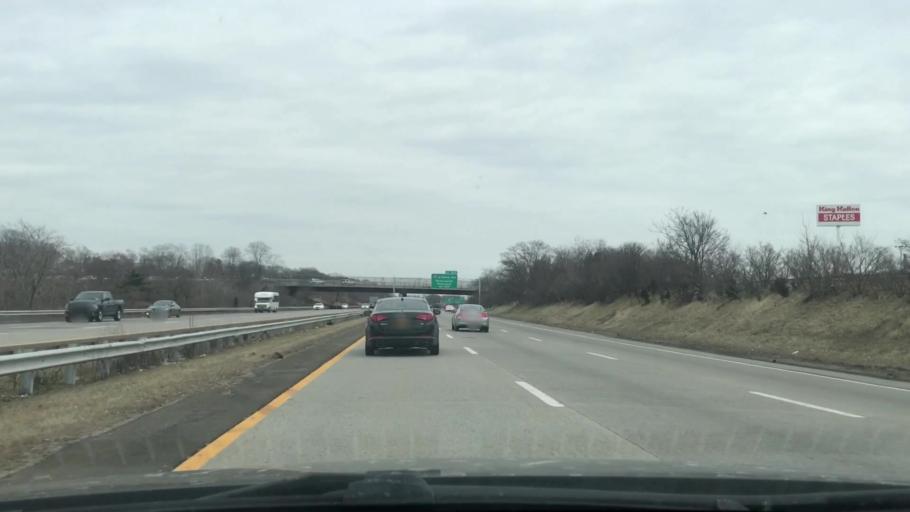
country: US
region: New York
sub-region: Suffolk County
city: Patchogue
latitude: 40.7767
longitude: -73.0326
